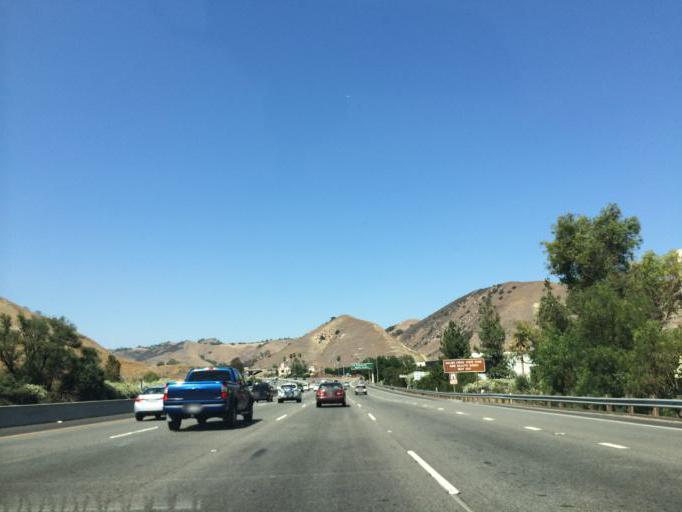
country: US
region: California
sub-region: Los Angeles County
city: Agoura
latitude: 34.1435
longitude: -118.7042
